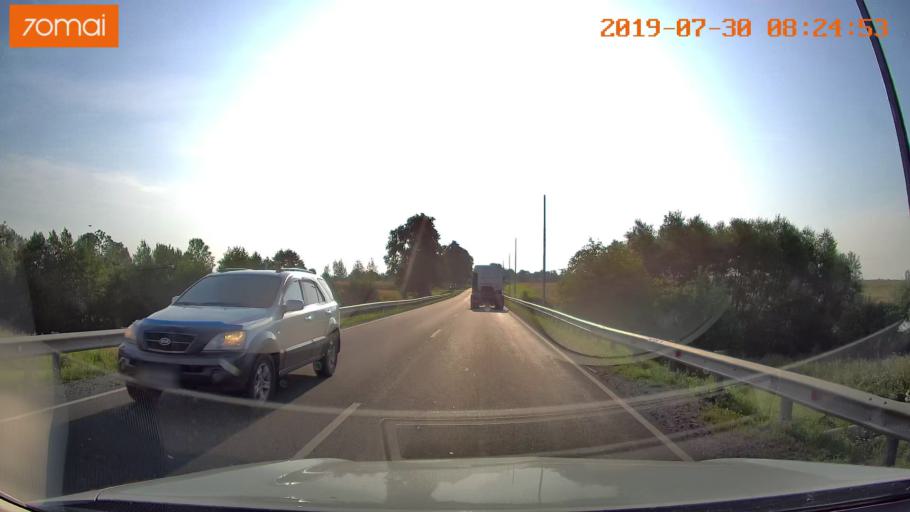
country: RU
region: Kaliningrad
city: Chernyakhovsk
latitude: 54.6238
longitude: 21.5679
